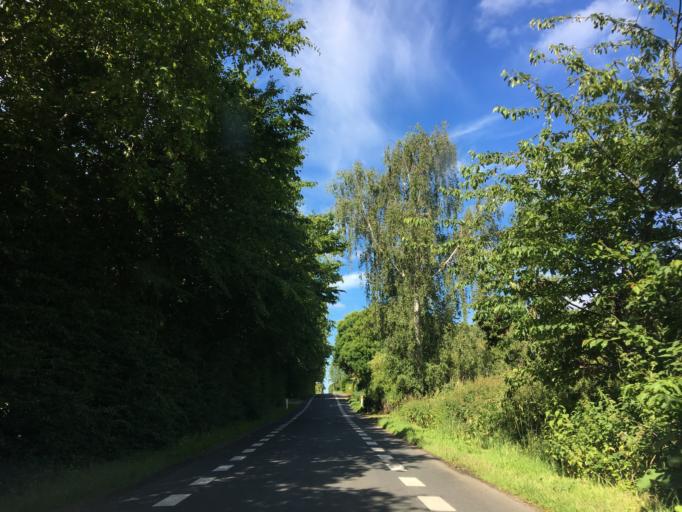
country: DK
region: South Denmark
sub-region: Svendborg Kommune
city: Thuro By
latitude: 55.0457
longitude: 10.6987
